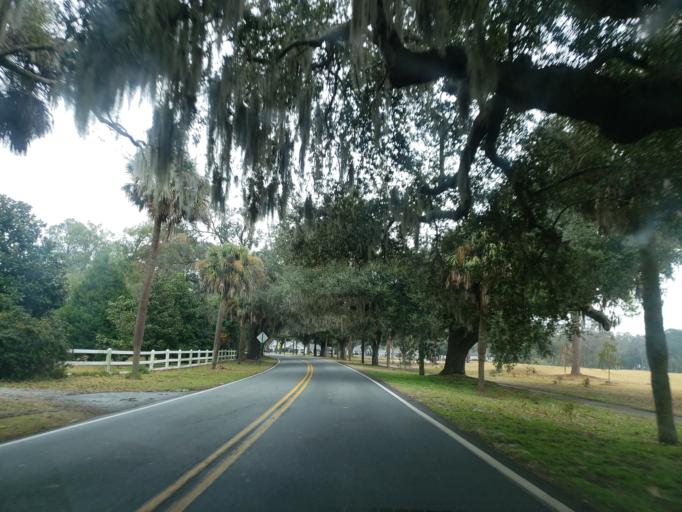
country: US
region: Georgia
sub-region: Chatham County
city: Wilmington Island
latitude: 32.0050
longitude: -80.9930
